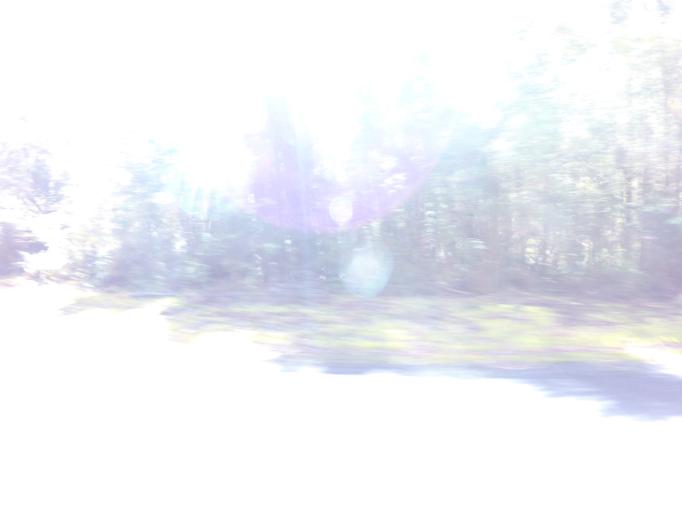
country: AU
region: Tasmania
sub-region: Huon Valley
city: Geeveston
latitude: -42.8201
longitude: 146.2884
